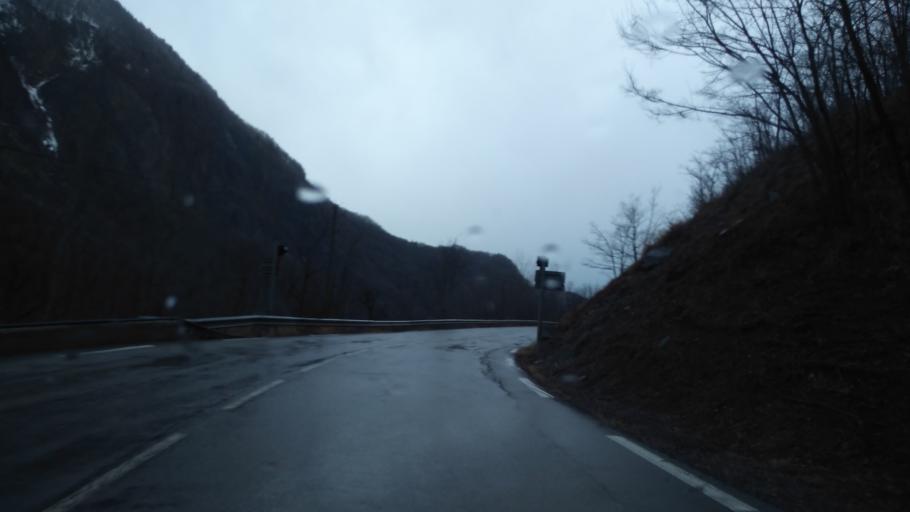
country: FR
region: Rhone-Alpes
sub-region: Departement de l'Isere
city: Mont-de-Lans
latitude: 45.0428
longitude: 6.1687
